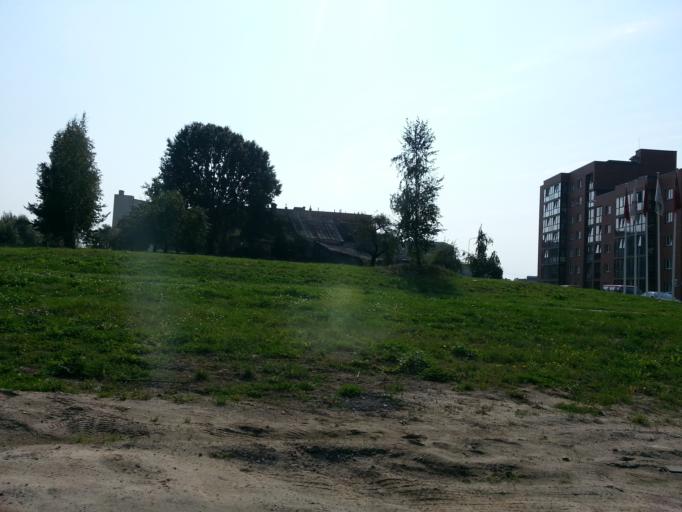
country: LT
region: Vilnius County
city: Pasilaiciai
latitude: 54.7343
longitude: 25.2186
